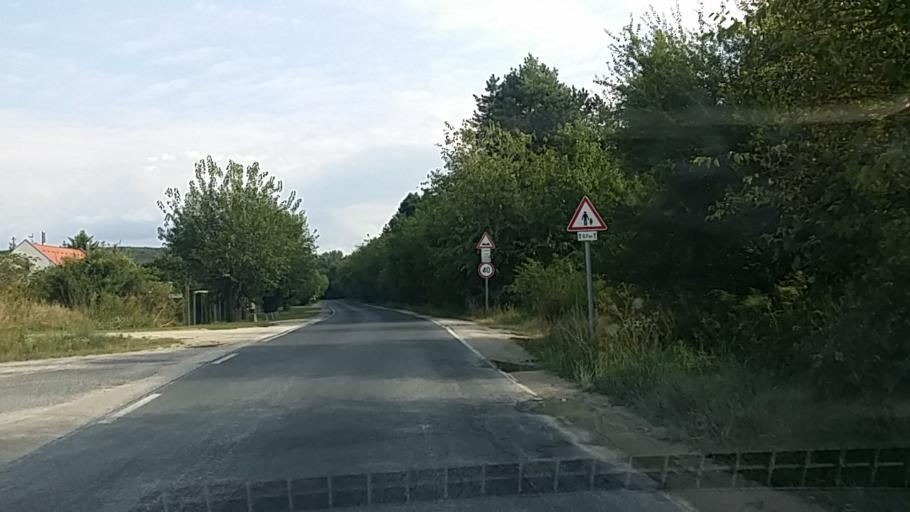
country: HU
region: Gyor-Moson-Sopron
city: Fertorakos
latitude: 47.7310
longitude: 16.6209
